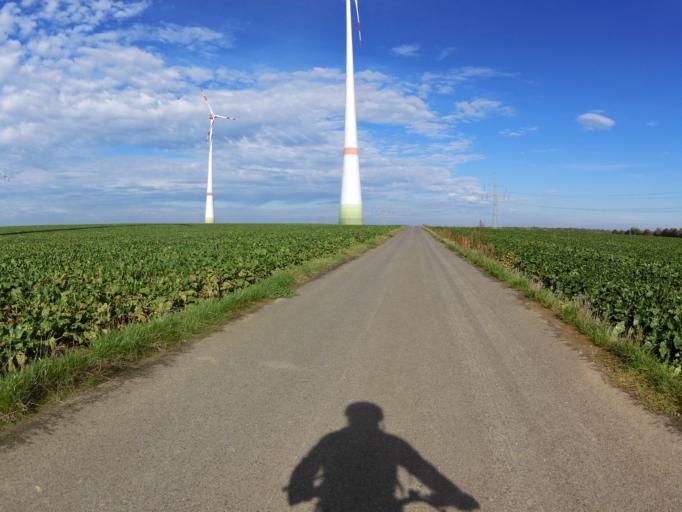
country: DE
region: Bavaria
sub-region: Regierungsbezirk Unterfranken
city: Sommerhausen
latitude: 49.7149
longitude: 10.0540
